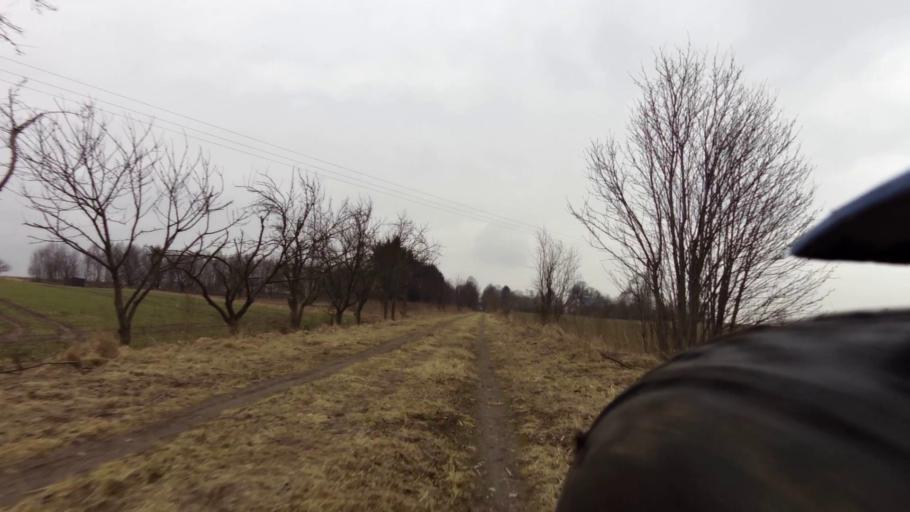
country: PL
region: West Pomeranian Voivodeship
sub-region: Powiat walecki
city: Walcz
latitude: 53.2512
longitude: 16.4773
